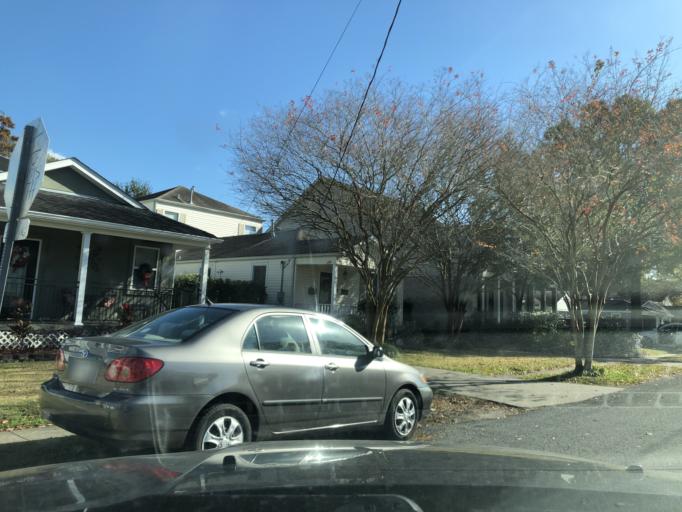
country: US
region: Louisiana
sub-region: Jefferson Parish
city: Metairie
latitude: 29.9861
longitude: -90.1589
